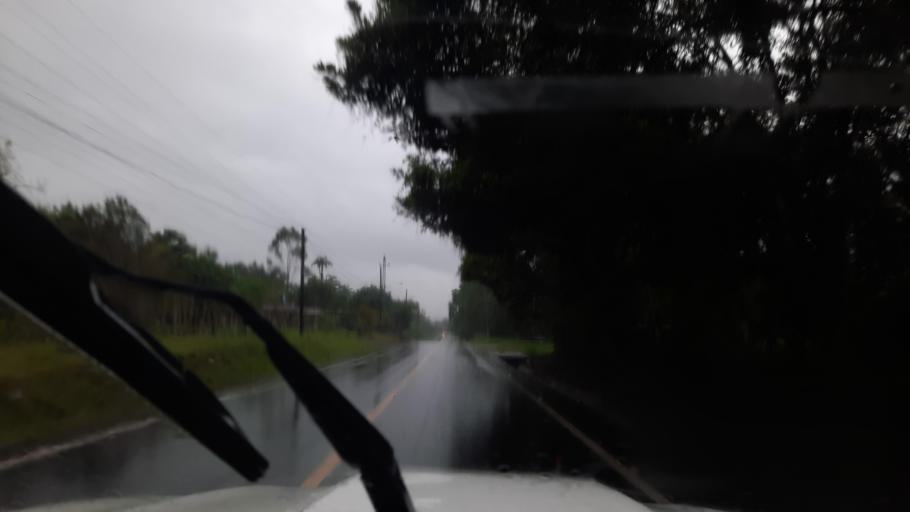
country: PA
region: Chiriqui
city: Sortova
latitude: 8.5847
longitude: -82.6371
